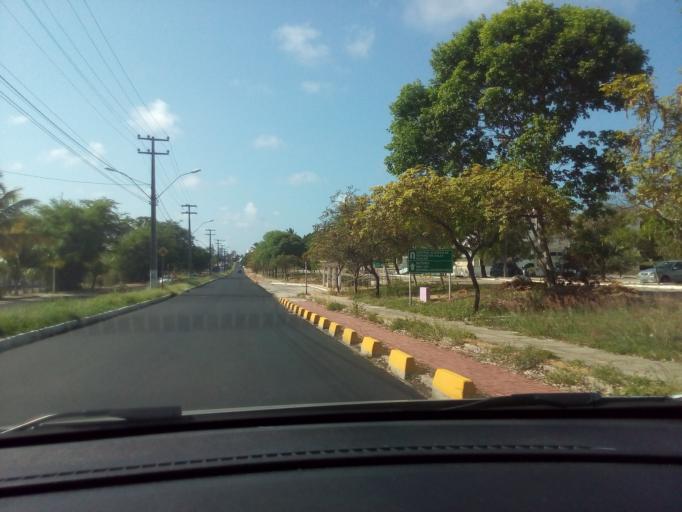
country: BR
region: Rio Grande do Norte
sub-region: Natal
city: Natal
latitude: -5.8426
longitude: -35.2030
